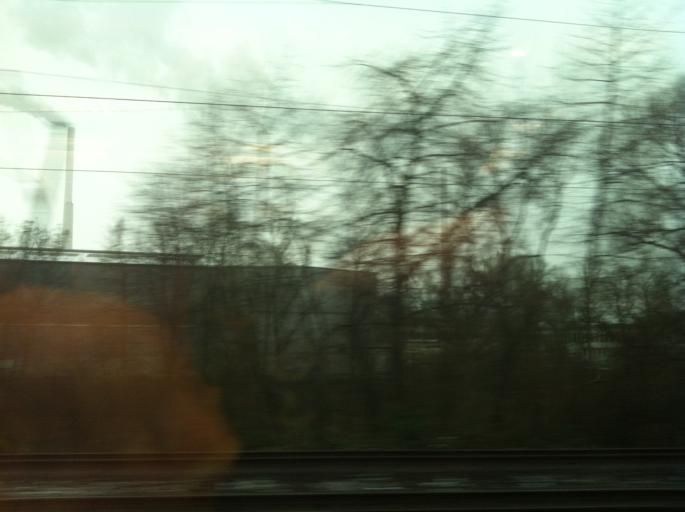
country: DE
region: Baden-Wuerttemberg
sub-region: Regierungsbezirk Stuttgart
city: Altbach
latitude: 48.7245
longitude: 9.3723
